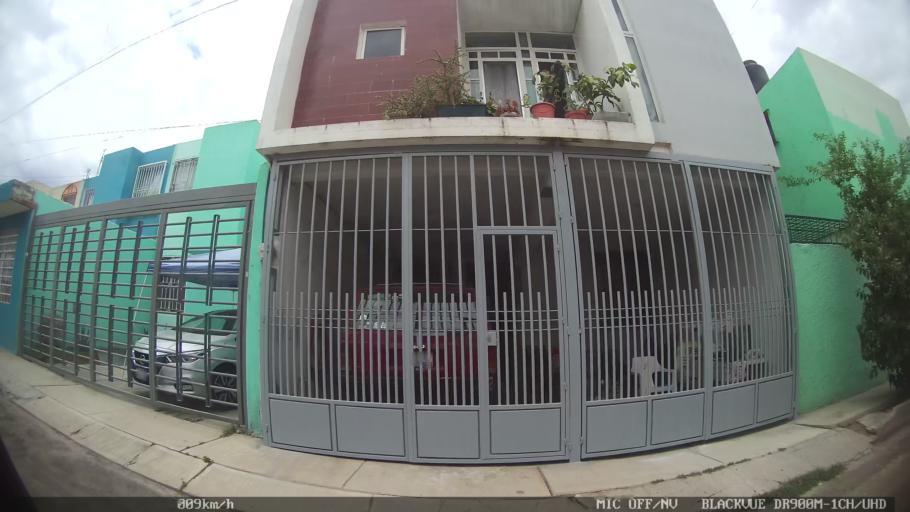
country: MX
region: Jalisco
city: Tonala
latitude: 20.6397
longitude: -103.2542
